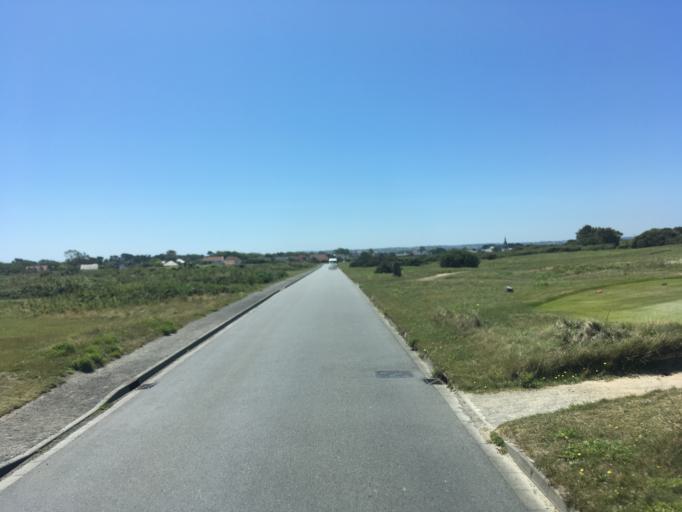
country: GG
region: St Peter Port
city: Saint Peter Port
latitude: 49.5029
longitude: -2.5330
